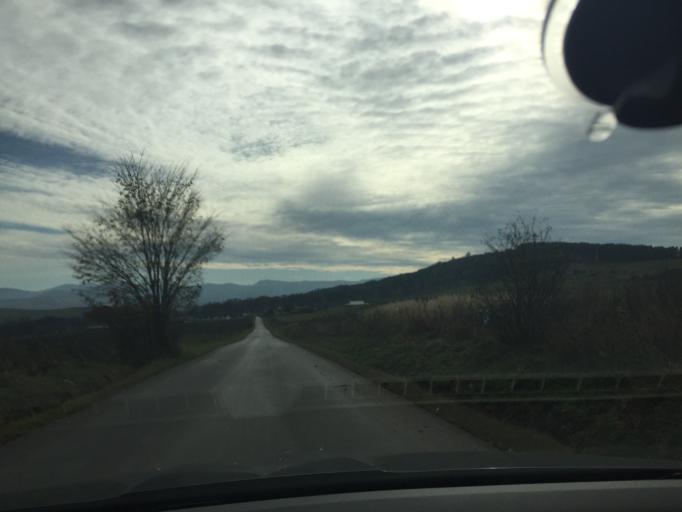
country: SK
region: Presovsky
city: Spisske Podhradie
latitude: 48.9981
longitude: 20.7794
